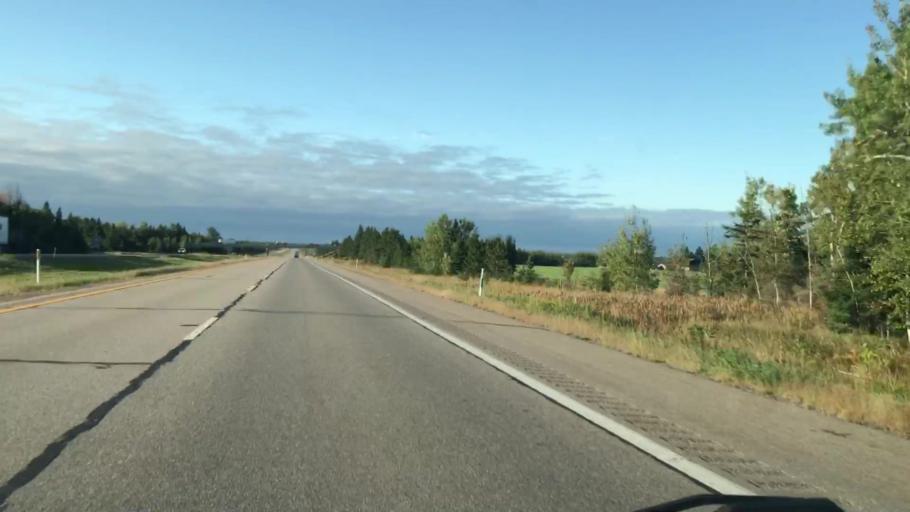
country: US
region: Michigan
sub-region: Chippewa County
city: Sault Ste. Marie
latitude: 46.4238
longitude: -84.3936
